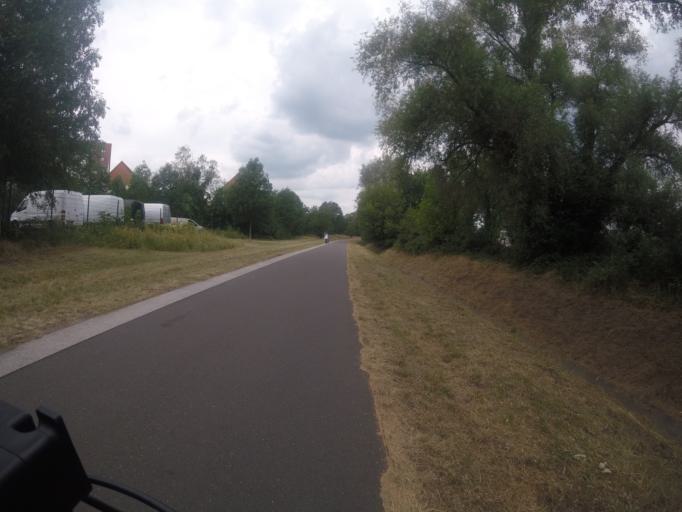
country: DE
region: Berlin
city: Wilhelmstadt
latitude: 52.5298
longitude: 13.1821
